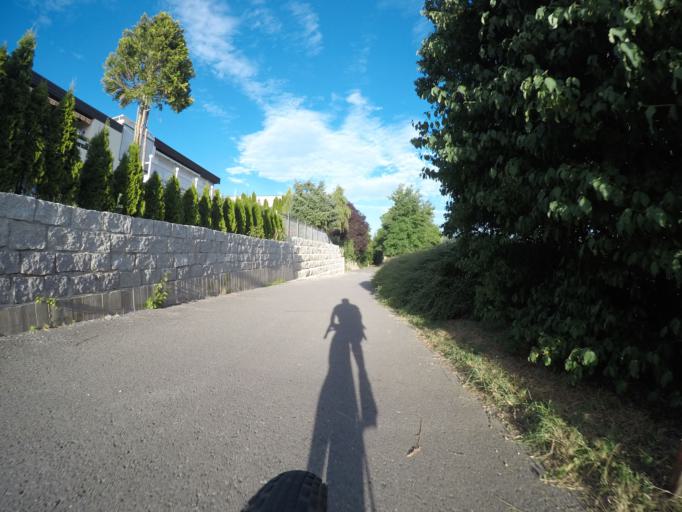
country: DE
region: Baden-Wuerttemberg
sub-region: Regierungsbezirk Stuttgart
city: Ehningen
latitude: 48.6915
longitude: 8.9598
